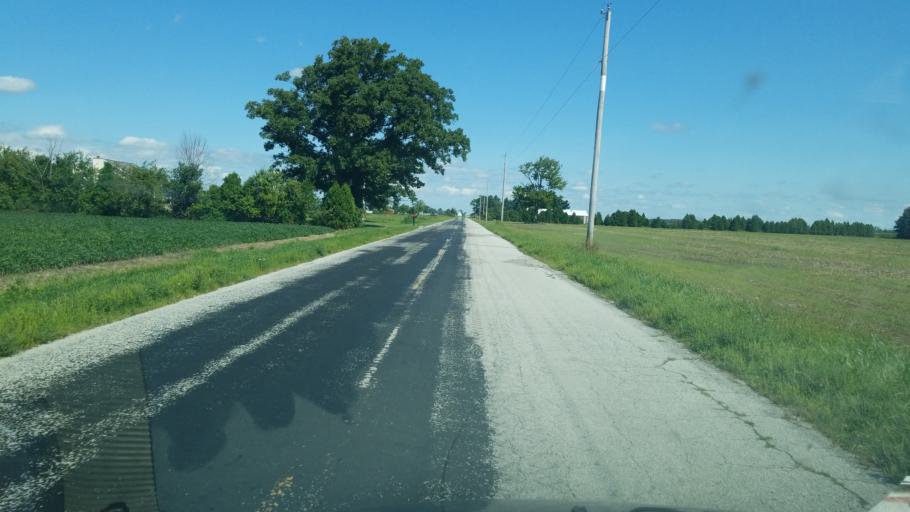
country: US
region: Ohio
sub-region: Henry County
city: Deshler
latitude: 41.2489
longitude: -83.8426
